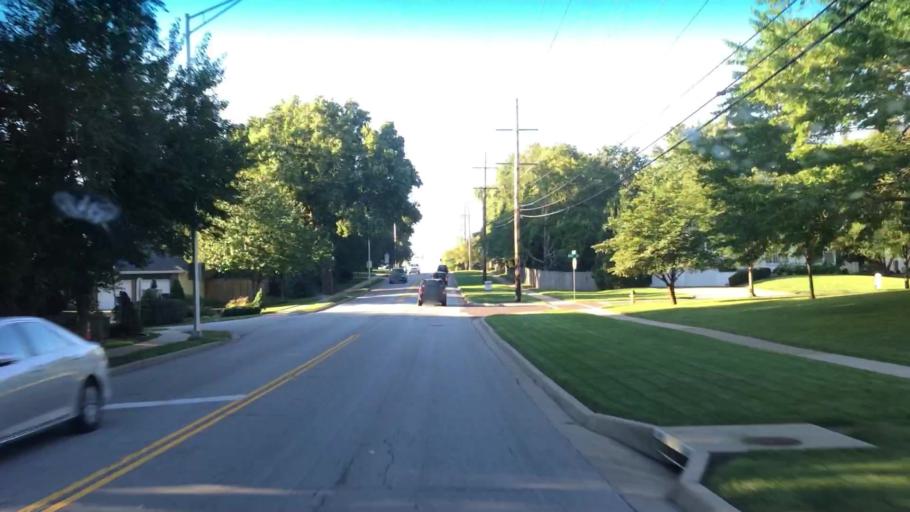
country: US
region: Kansas
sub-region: Johnson County
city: Overland Park
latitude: 38.9736
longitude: -94.6490
